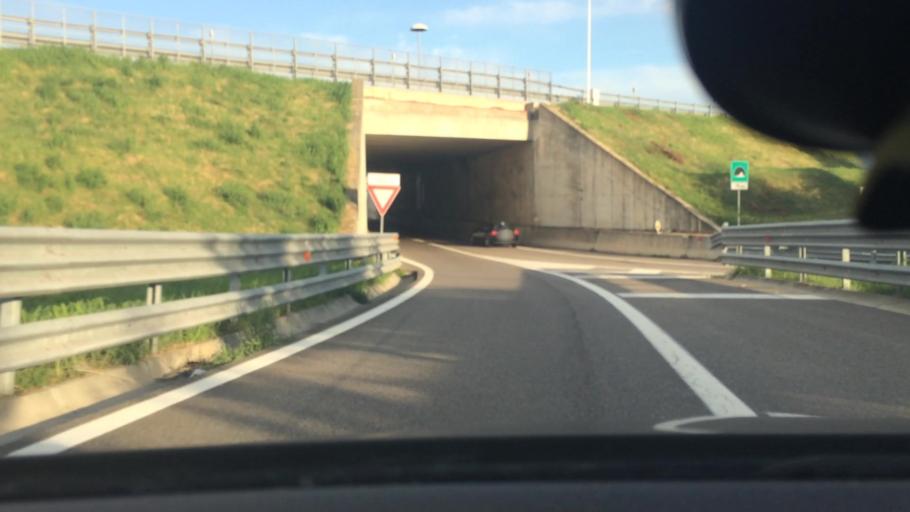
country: IT
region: Lombardy
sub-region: Citta metropolitana di Milano
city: Rho
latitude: 45.5247
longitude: 9.0598
